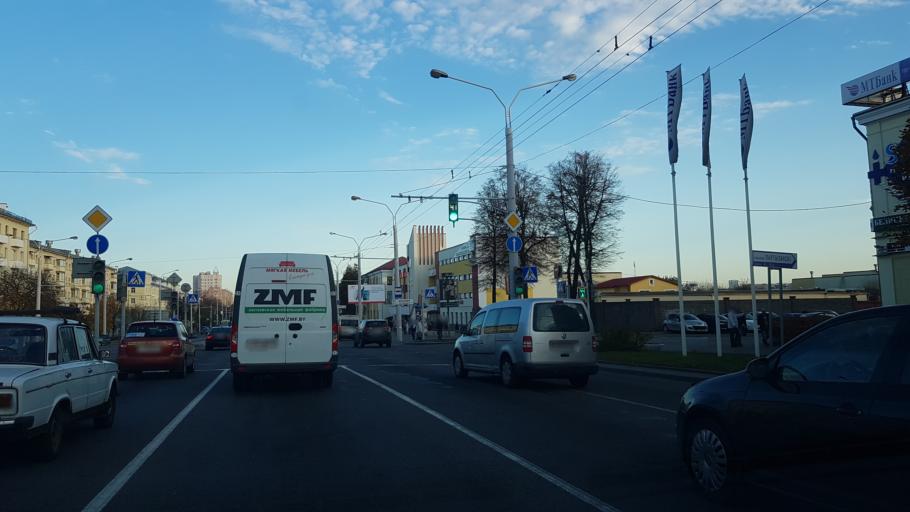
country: BY
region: Minsk
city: Minsk
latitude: 53.8859
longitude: 27.5841
